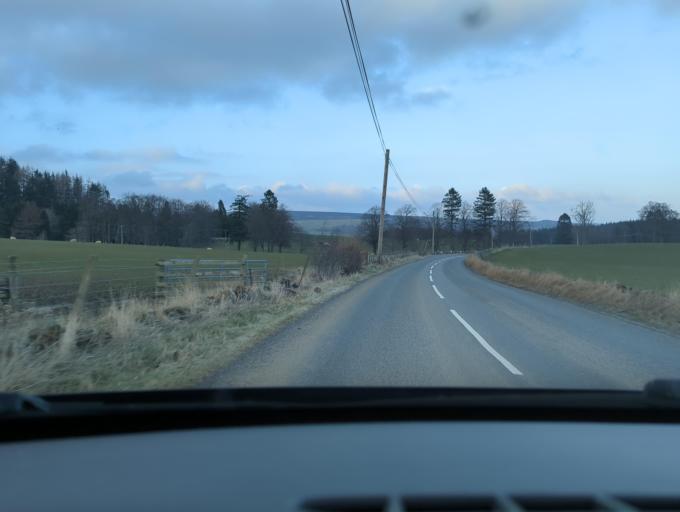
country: GB
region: Scotland
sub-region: Perth and Kinross
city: Aberfeldy
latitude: 56.5302
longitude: -3.7197
